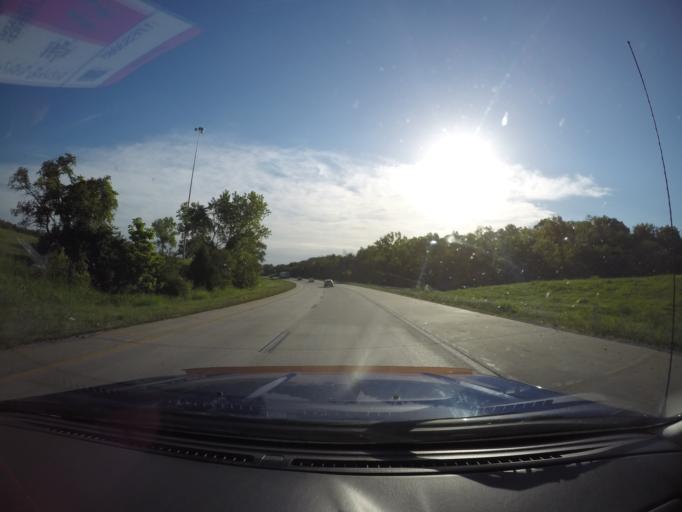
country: US
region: Kansas
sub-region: Wyandotte County
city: Kansas City
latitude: 39.1470
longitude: -94.6562
